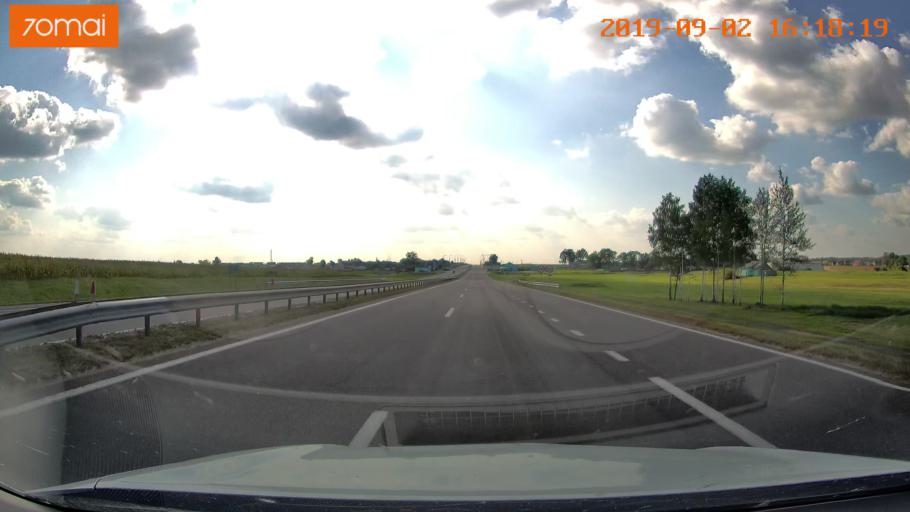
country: BY
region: Minsk
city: Chervyen'
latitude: 53.7307
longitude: 28.4440
